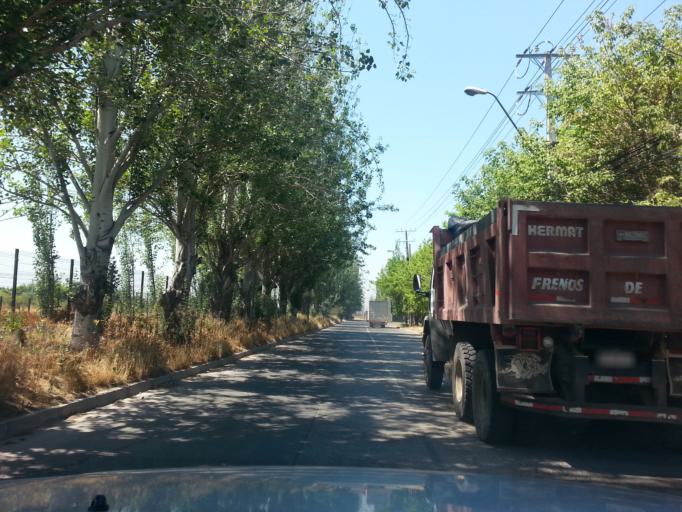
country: CL
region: Santiago Metropolitan
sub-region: Provincia de Chacabuco
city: Chicureo Abajo
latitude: -33.3543
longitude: -70.6929
